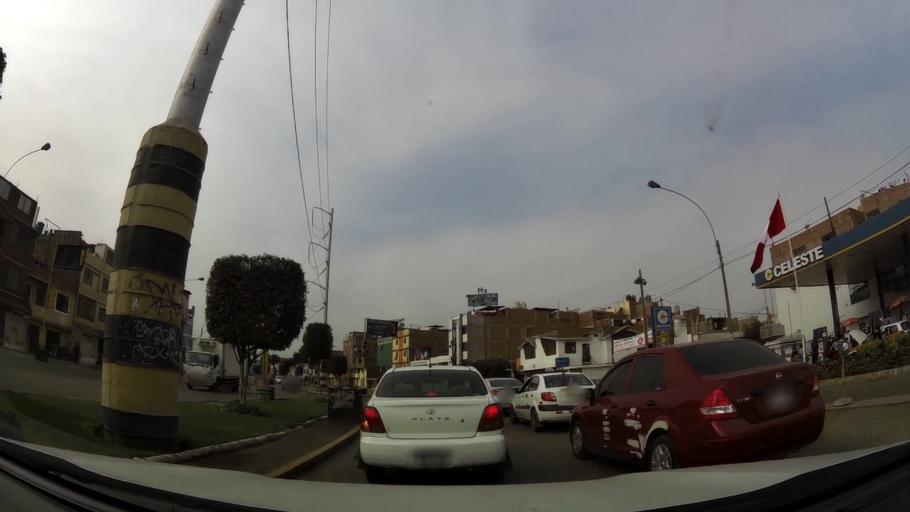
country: PE
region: Callao
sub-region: Callao
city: Callao
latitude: -12.0358
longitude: -77.0975
